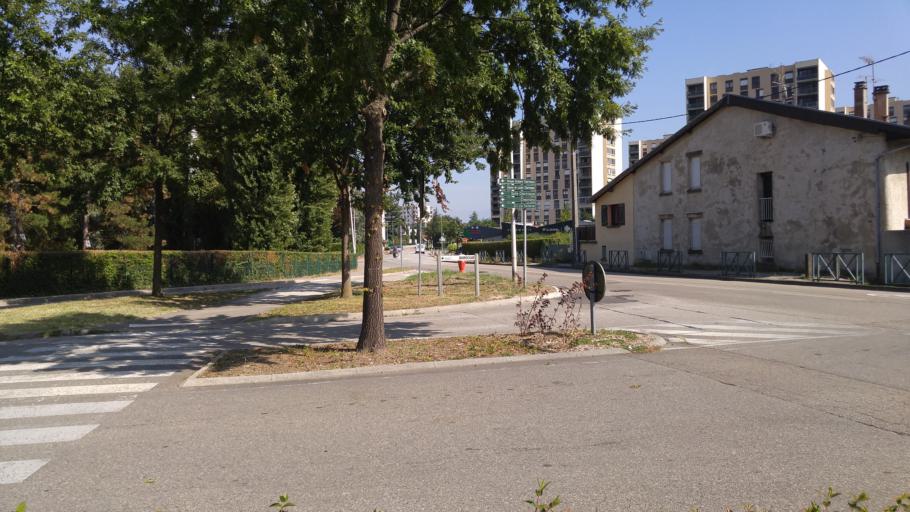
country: FR
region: Rhone-Alpes
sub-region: Departement de l'Isere
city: Seyssinet-Pariset
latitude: 45.1698
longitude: 5.6926
